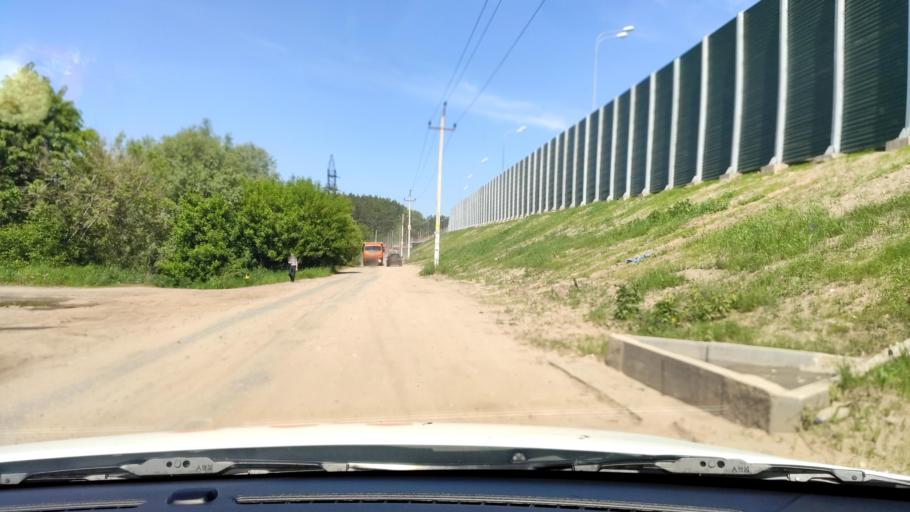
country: RU
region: Tatarstan
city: Osinovo
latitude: 55.8224
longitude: 48.8449
